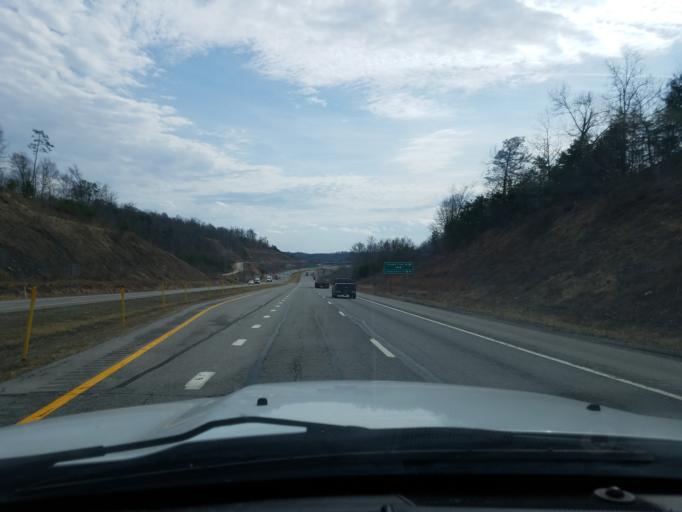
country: US
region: West Virginia
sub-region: Putnam County
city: Teays Valley
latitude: 38.4651
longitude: -81.9083
